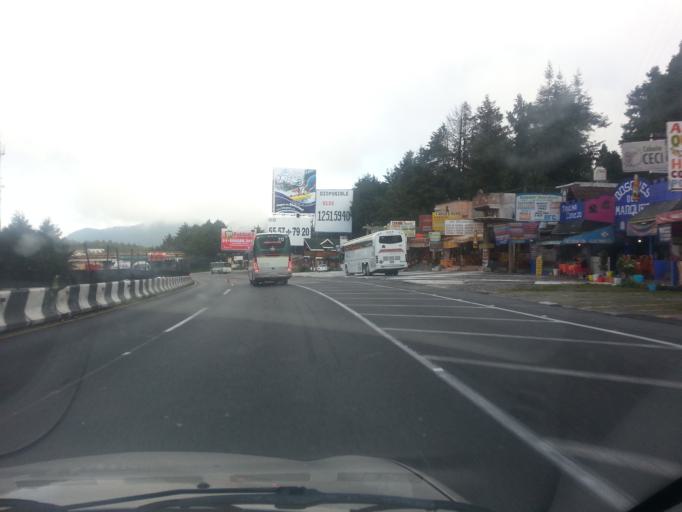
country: MX
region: Mexico City
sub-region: Cuajimalpa de Morelos
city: San Lorenzo Acopilco
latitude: 19.3017
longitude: -99.3679
